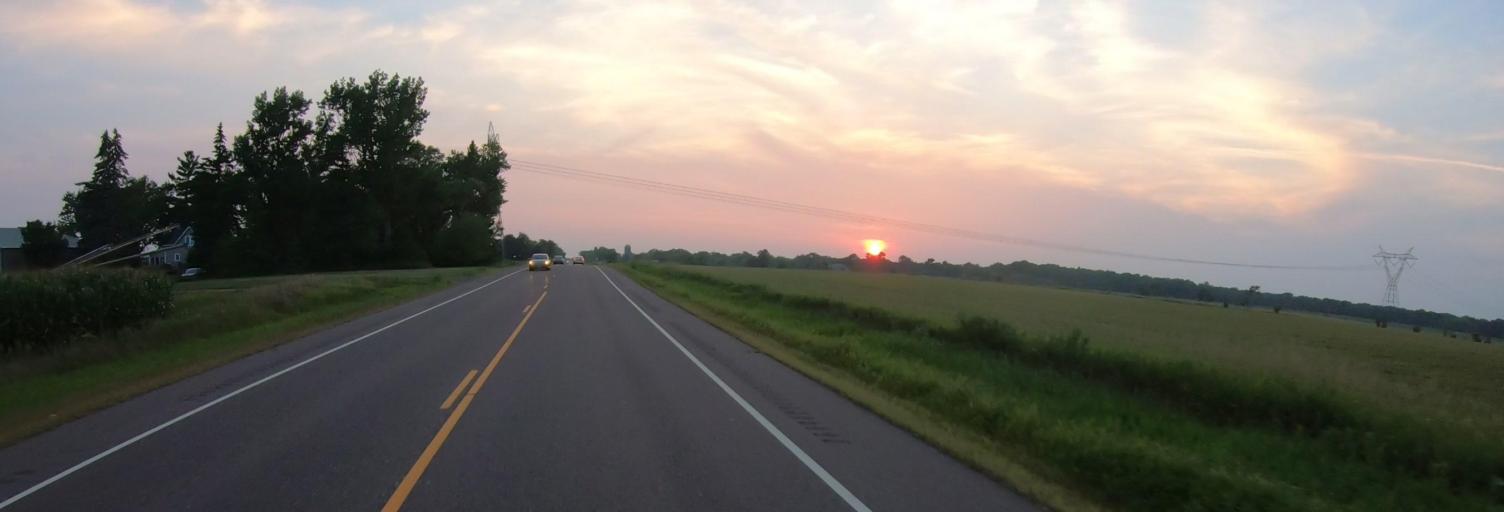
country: US
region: Minnesota
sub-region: Pine County
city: Rock Creek
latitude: 45.7734
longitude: -92.9059
